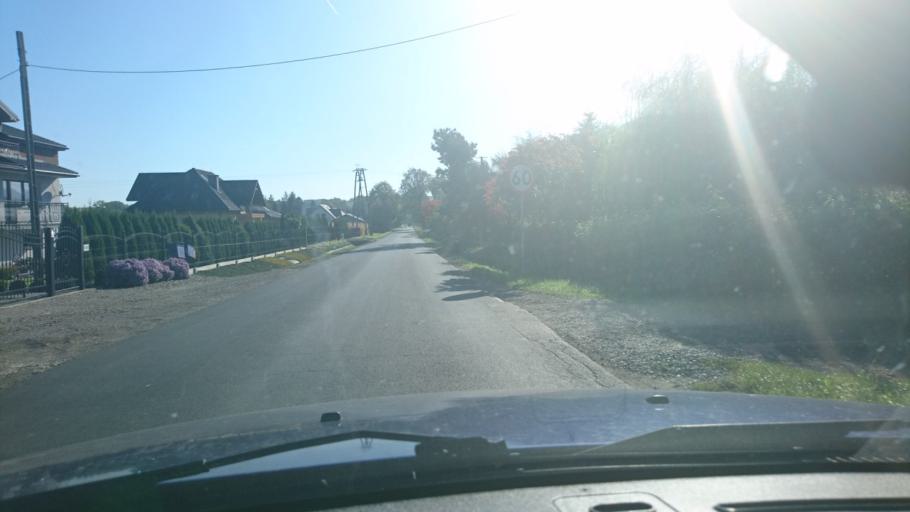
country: PL
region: Silesian Voivodeship
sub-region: Powiat bielski
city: Bronow
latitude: 49.8526
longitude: 18.9352
